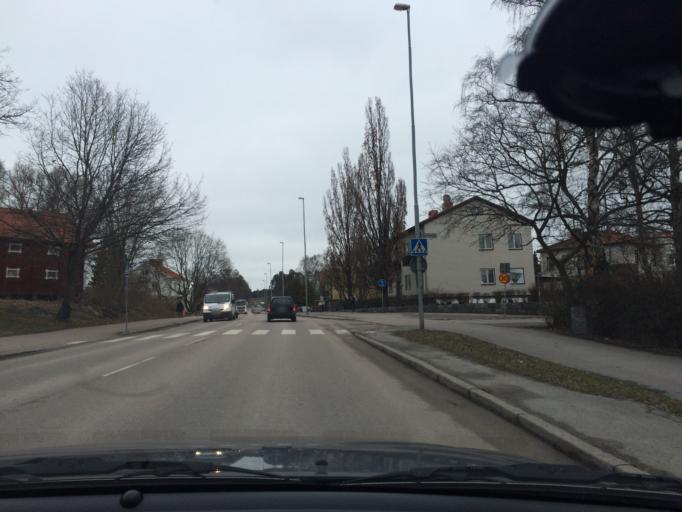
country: SE
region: Vaestmanland
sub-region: Vasteras
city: Vasteras
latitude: 59.6201
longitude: 16.5452
